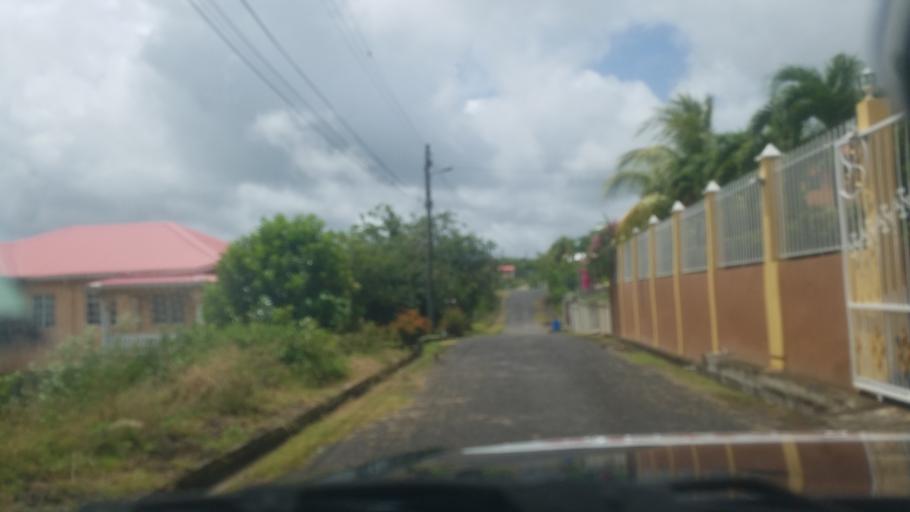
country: LC
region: Laborie Quarter
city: Laborie
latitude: 13.7486
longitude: -60.9769
